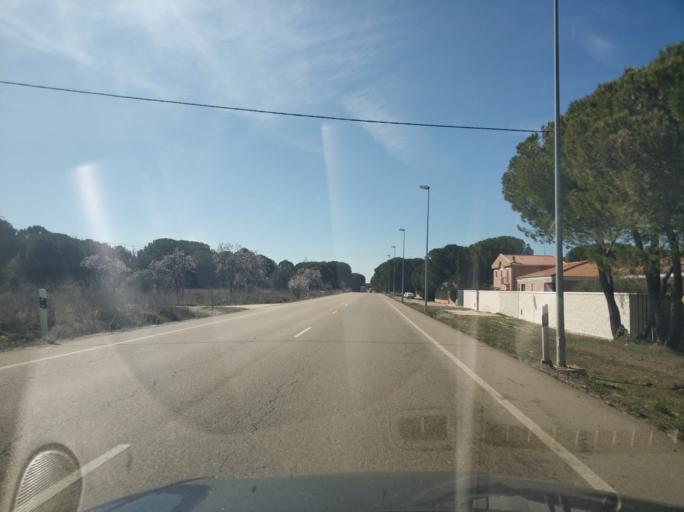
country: ES
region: Castille and Leon
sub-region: Provincia de Valladolid
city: Tudela de Duero
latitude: 41.5731
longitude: -4.5857
